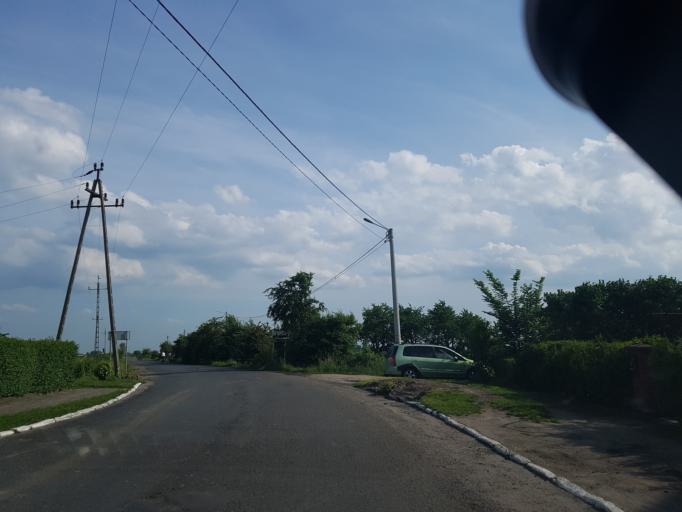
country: PL
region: Lower Silesian Voivodeship
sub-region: Powiat olawski
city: Wierzbno
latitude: 50.9079
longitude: 17.1246
